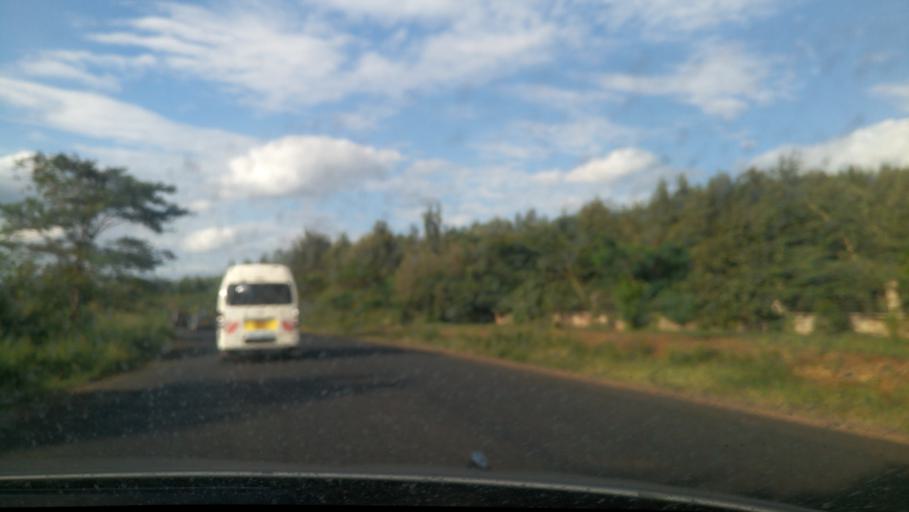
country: KE
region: Murang'a District
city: Maragua
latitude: -0.7725
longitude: 37.1516
